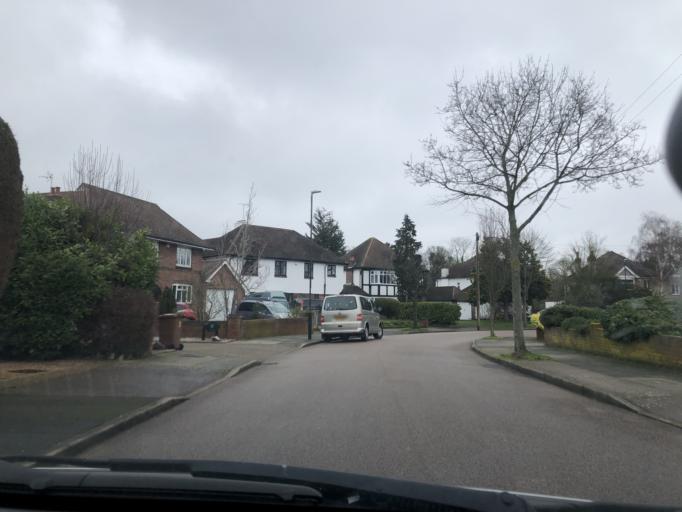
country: GB
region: England
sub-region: Greater London
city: Bexley
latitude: 51.4403
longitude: 0.1625
